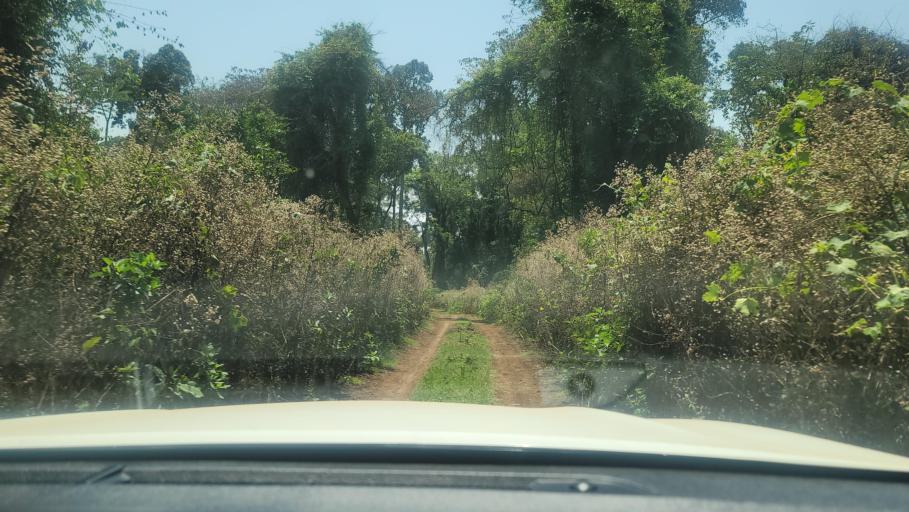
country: ET
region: Southern Nations, Nationalities, and People's Region
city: Bonga
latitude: 7.5502
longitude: 36.1737
